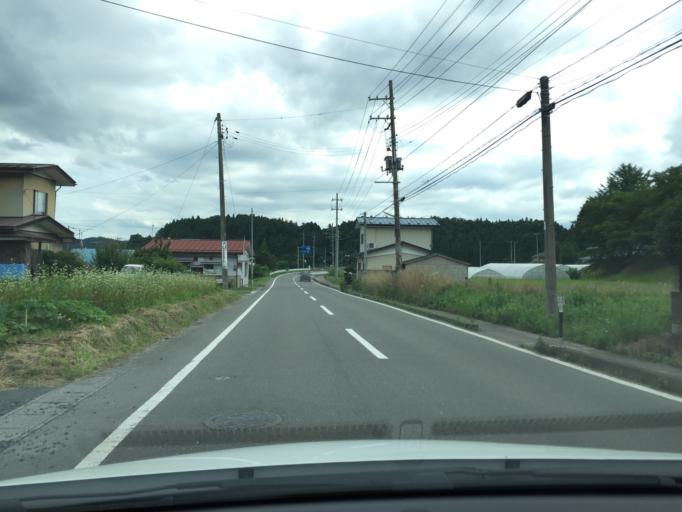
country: JP
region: Fukushima
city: Sukagawa
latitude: 37.3001
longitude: 140.2109
